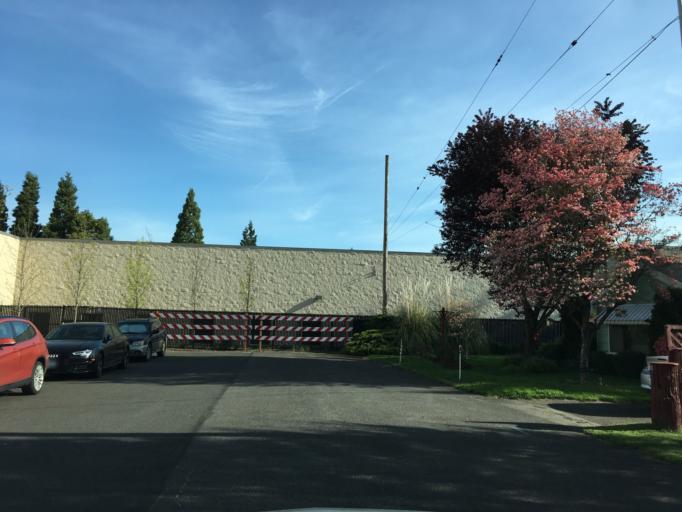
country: US
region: Oregon
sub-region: Multnomah County
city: Lents
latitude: 45.5347
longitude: -122.5566
